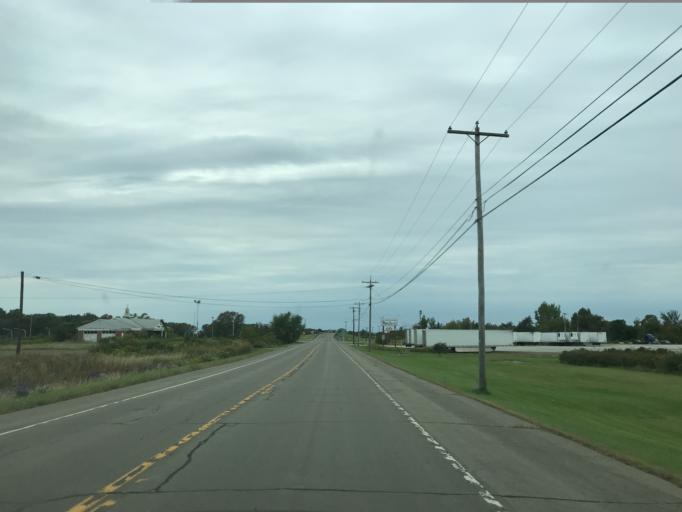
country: US
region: Pennsylvania
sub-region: Erie County
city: North East
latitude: 42.2580
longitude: -79.7417
